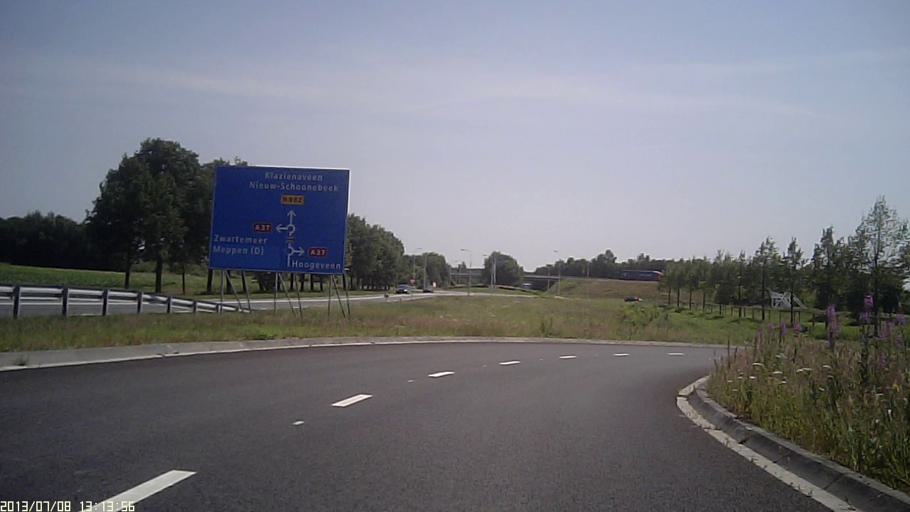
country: NL
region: Drenthe
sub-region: Gemeente Emmen
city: Klazienaveen
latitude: 52.7378
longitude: 6.9719
